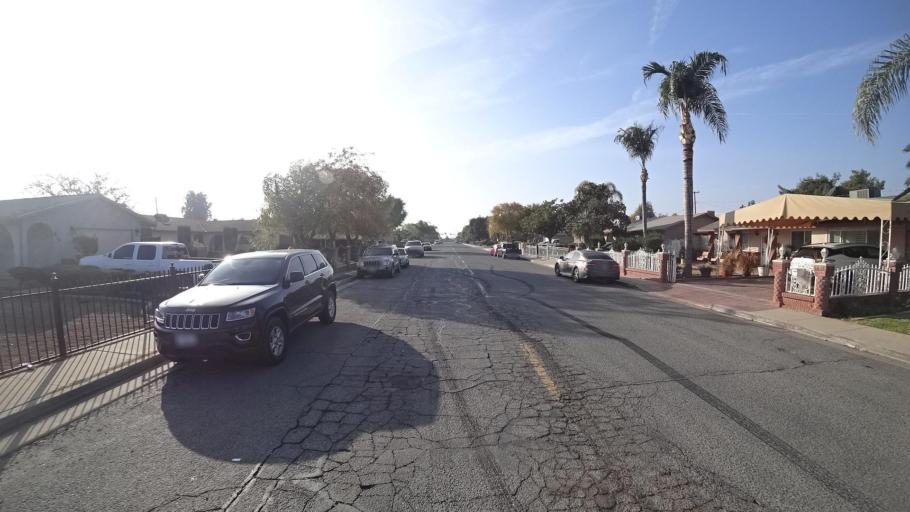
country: US
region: California
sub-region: Kern County
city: McFarland
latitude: 35.6770
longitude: -119.2187
